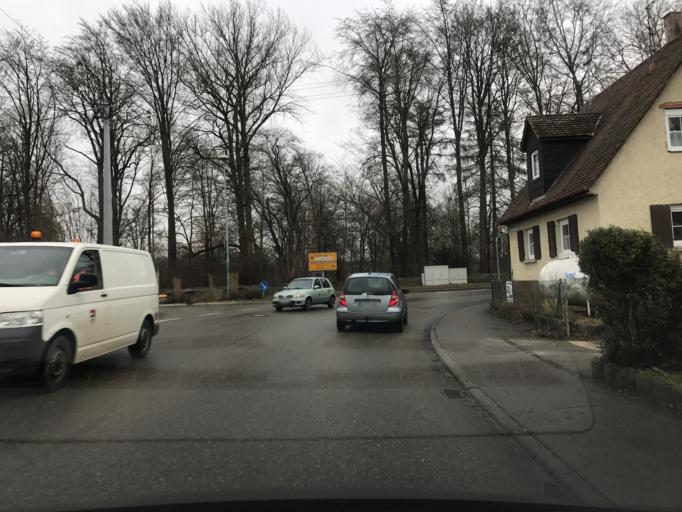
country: DE
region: Baden-Wuerttemberg
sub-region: Tuebingen Region
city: Opfingen
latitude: 48.2649
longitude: 9.8293
